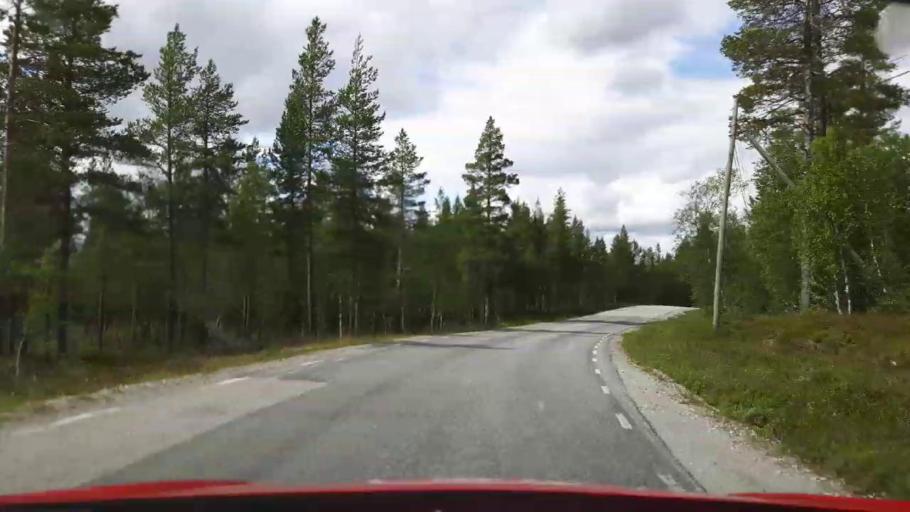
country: NO
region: Hedmark
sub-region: Engerdal
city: Engerdal
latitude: 62.4203
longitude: 12.6929
